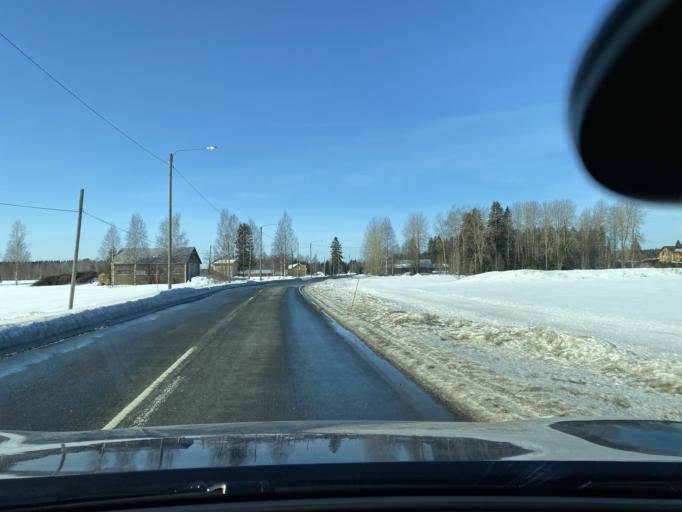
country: FI
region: Central Finland
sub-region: Joutsa
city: Joutsa
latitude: 61.8109
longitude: 25.9511
